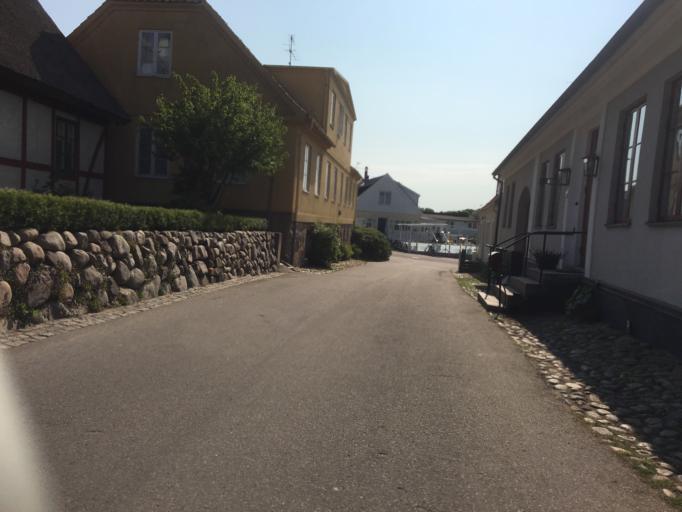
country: SE
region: Skane
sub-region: Hoganas Kommun
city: Hoganas
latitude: 56.1436
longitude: 12.5766
